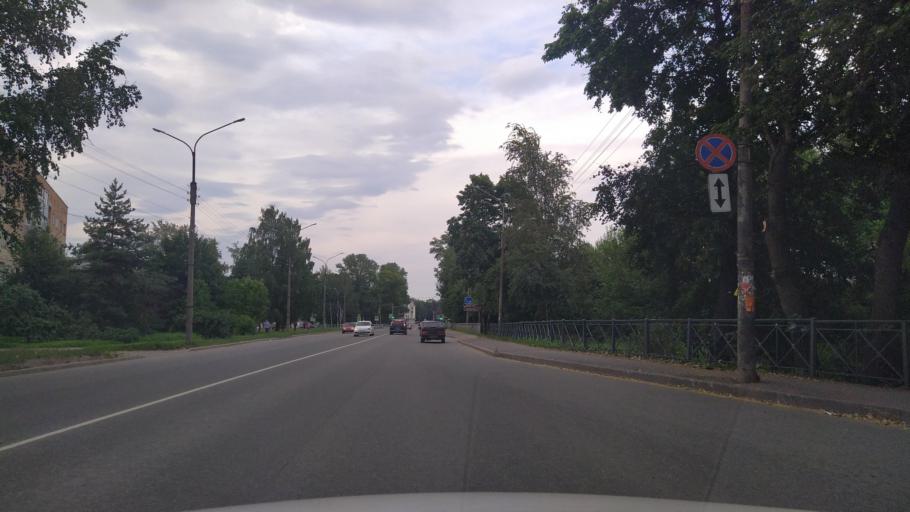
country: RU
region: Novgorod
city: Velikiy Novgorod
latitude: 58.5206
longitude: 31.2539
